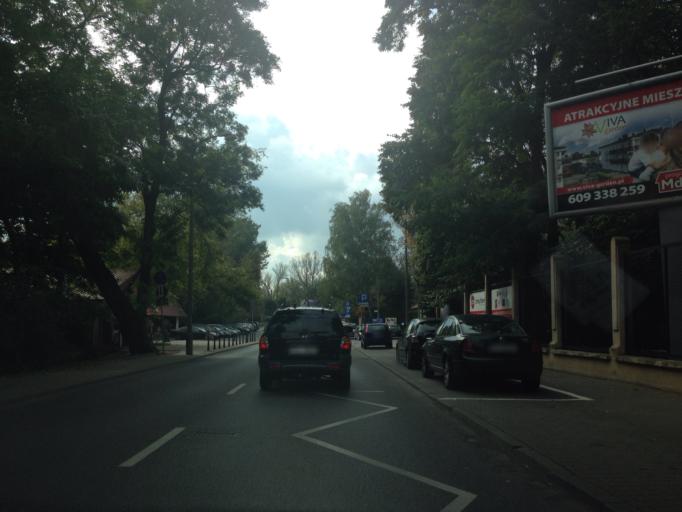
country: PL
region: Masovian Voivodeship
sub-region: Warszawa
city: Praga Polnoc
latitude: 52.2546
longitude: 21.0247
